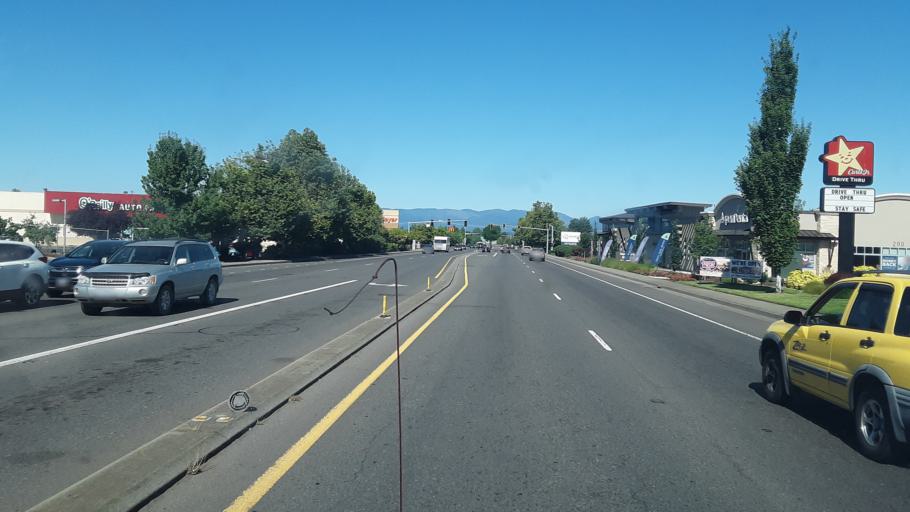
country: US
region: Oregon
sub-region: Josephine County
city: Fruitdale
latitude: 42.4367
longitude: -123.3031
